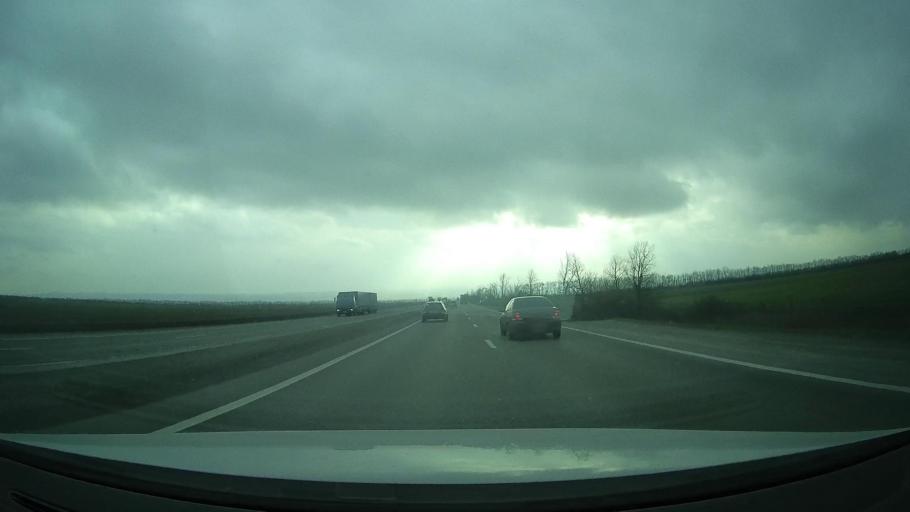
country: RU
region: Rostov
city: Grushevskaya
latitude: 47.4966
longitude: 39.9705
